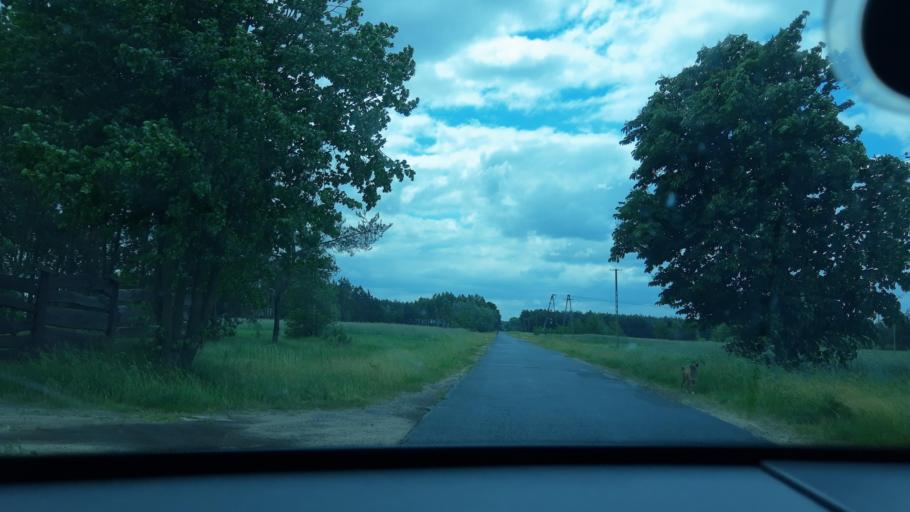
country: PL
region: Lodz Voivodeship
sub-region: Powiat sieradzki
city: Burzenin
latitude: 51.4932
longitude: 18.8447
